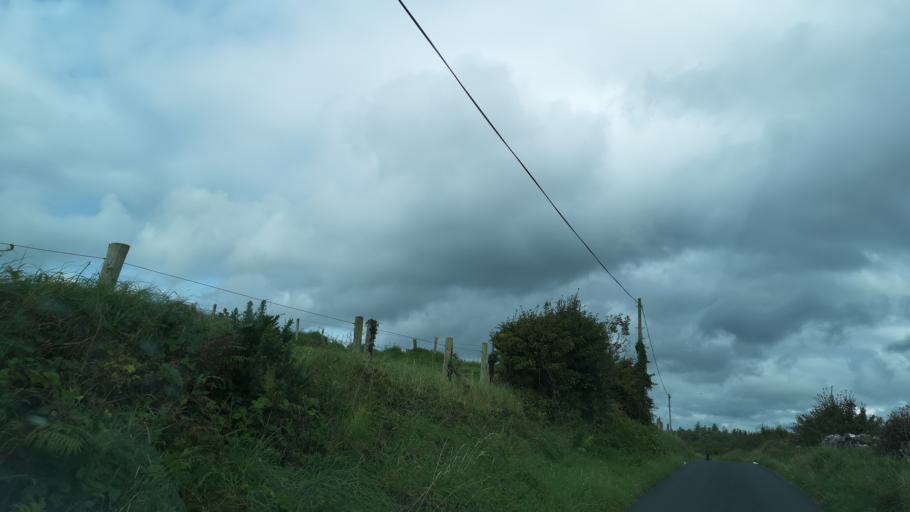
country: IE
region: Connaught
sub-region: County Galway
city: Athenry
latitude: 53.2801
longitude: -8.6694
